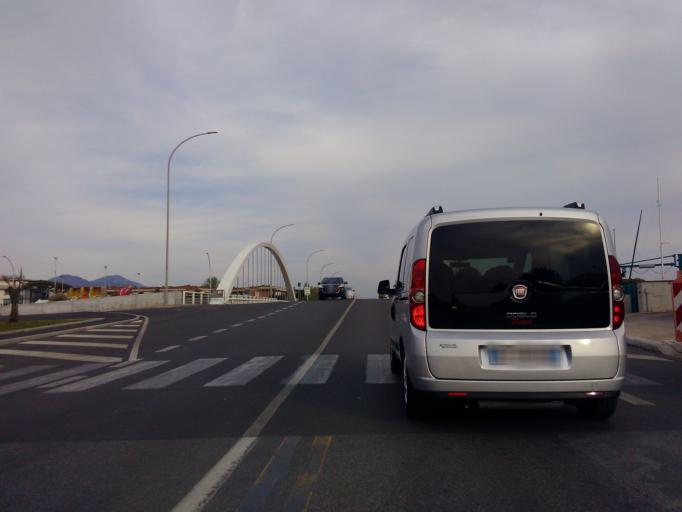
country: IT
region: Tuscany
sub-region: Provincia di Massa-Carrara
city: Massa
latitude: 44.0045
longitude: 10.1043
